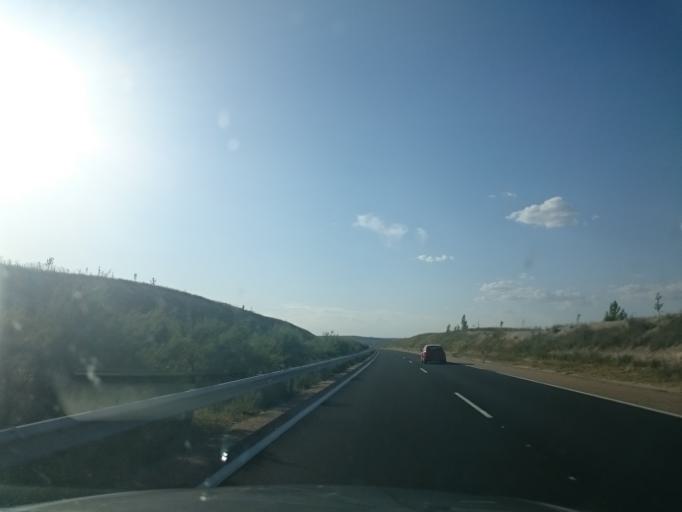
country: ES
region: Castille and Leon
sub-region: Provincia de Burgos
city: Villalbilla de Burgos
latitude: 42.3253
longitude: -3.7694
